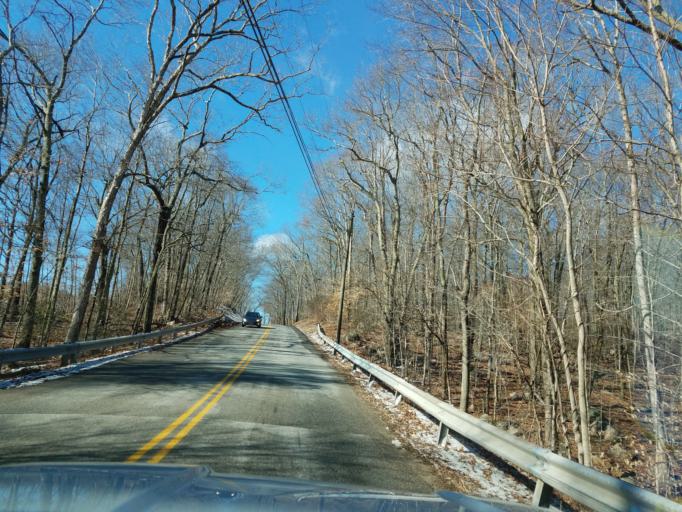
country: US
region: Connecticut
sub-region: New London County
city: Old Mystic
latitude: 41.4586
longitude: -71.9347
